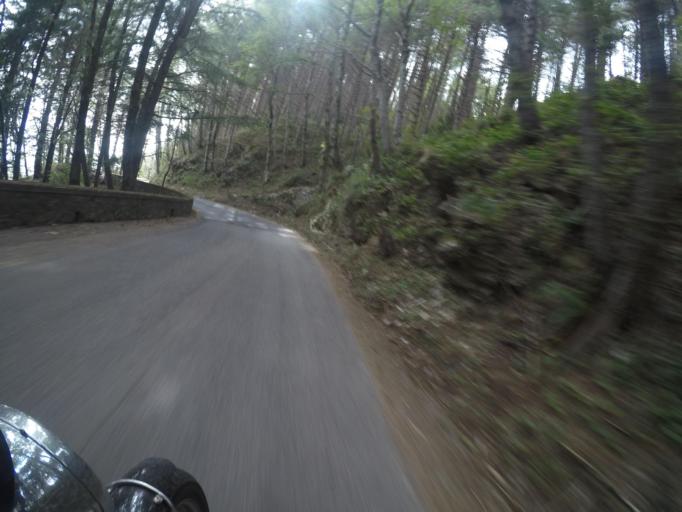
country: IT
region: Tuscany
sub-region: Provincia di Massa-Carrara
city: Carrara
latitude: 44.1219
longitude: 10.1102
